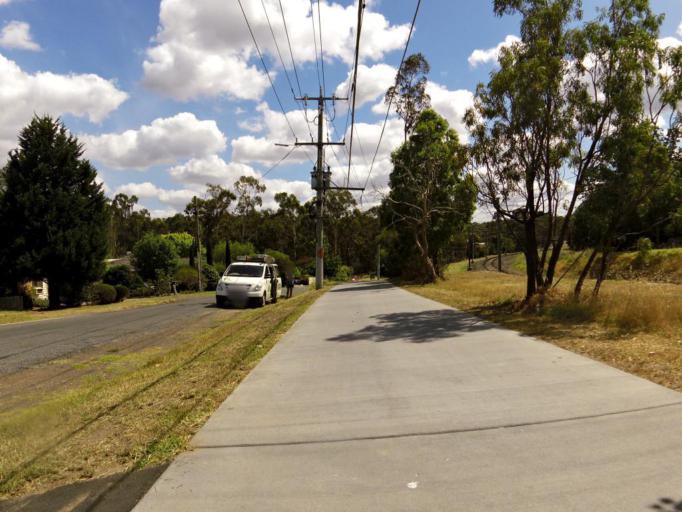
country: AU
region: Victoria
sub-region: Nillumbik
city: Eltham North
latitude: -37.7077
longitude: 145.1486
